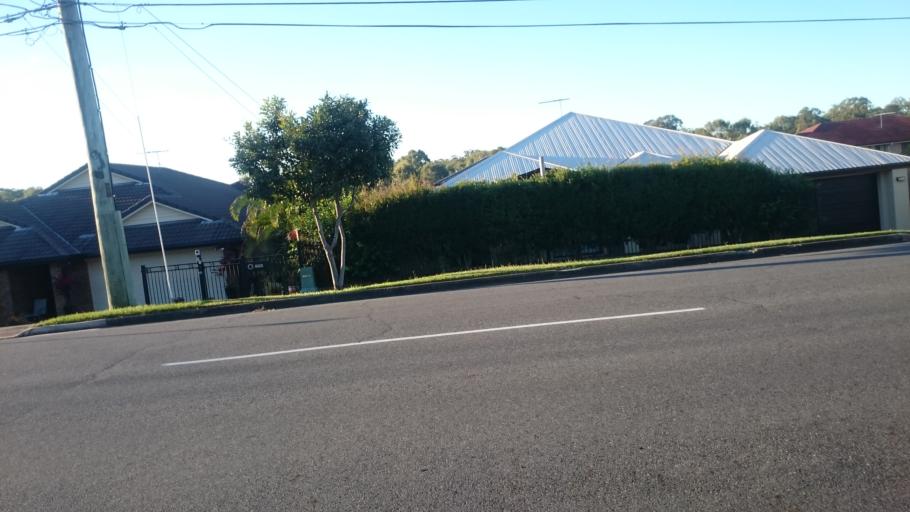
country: AU
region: Queensland
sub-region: Brisbane
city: Manly West
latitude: -27.4673
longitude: 153.1841
